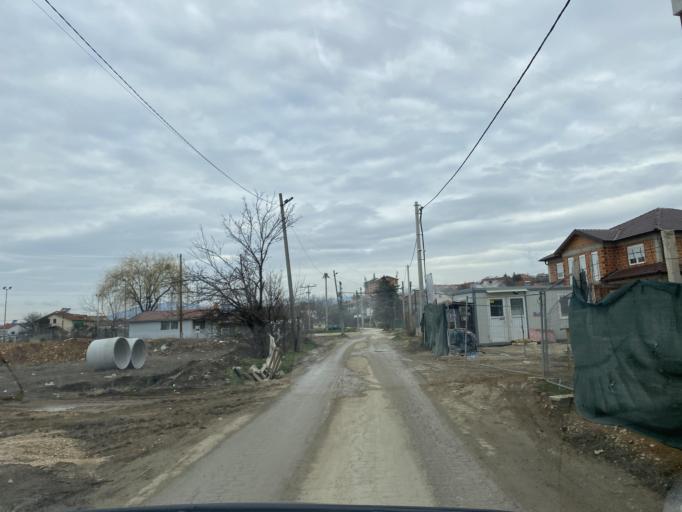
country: MK
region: Butel
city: Butel
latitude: 42.0423
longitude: 21.4605
